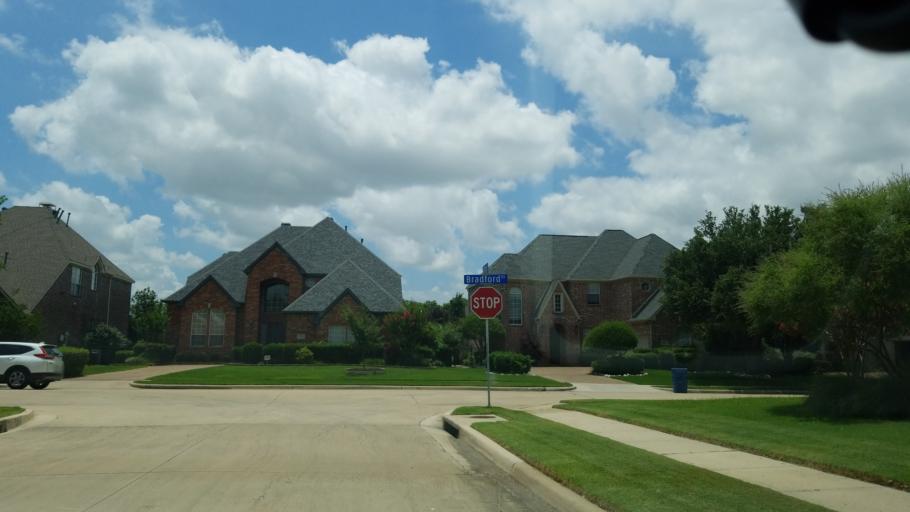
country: US
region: Texas
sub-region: Dallas County
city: Carrollton
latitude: 32.9625
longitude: -96.9518
